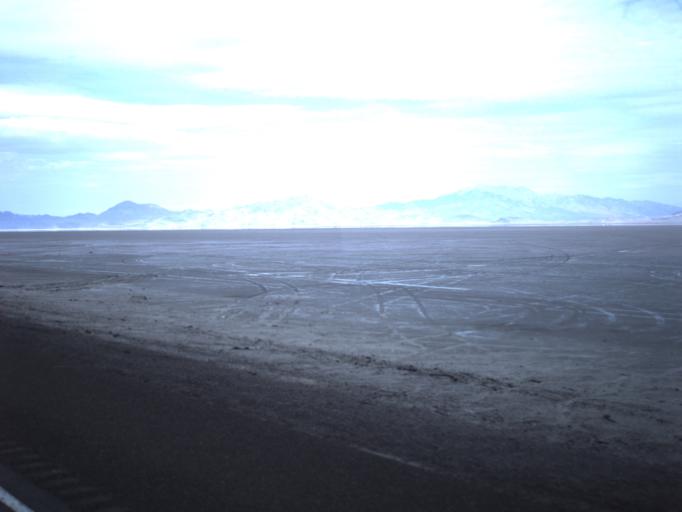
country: US
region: Utah
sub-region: Tooele County
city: Wendover
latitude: 40.7371
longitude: -113.7397
